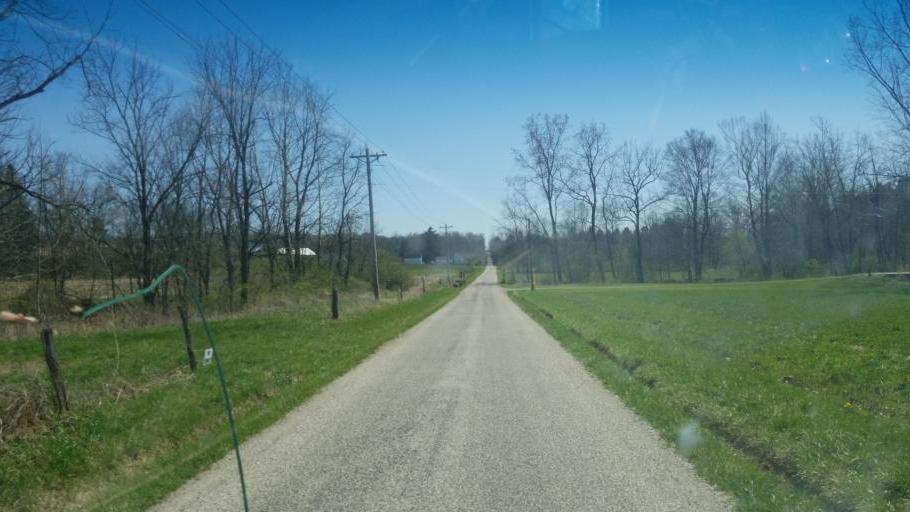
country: US
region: Ohio
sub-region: Ashland County
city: Ashland
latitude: 40.8349
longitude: -82.3877
